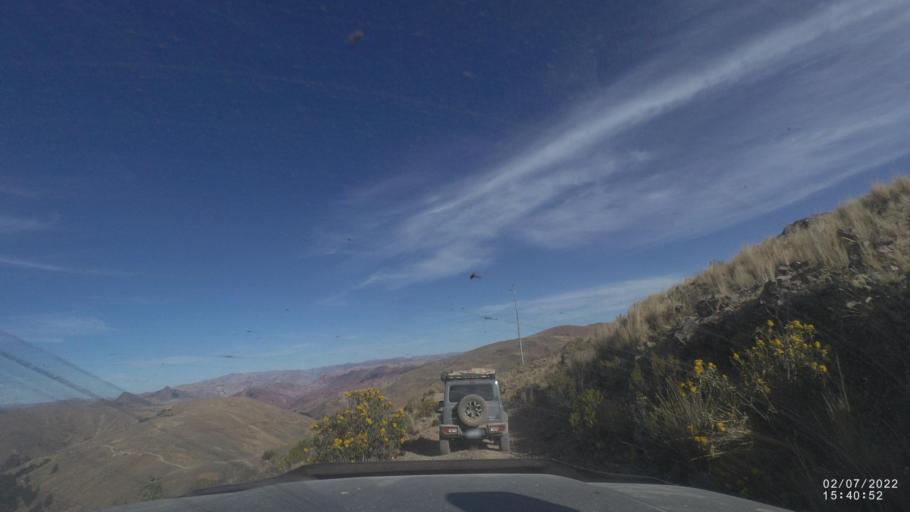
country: BO
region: Cochabamba
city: Irpa Irpa
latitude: -17.8994
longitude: -66.4103
